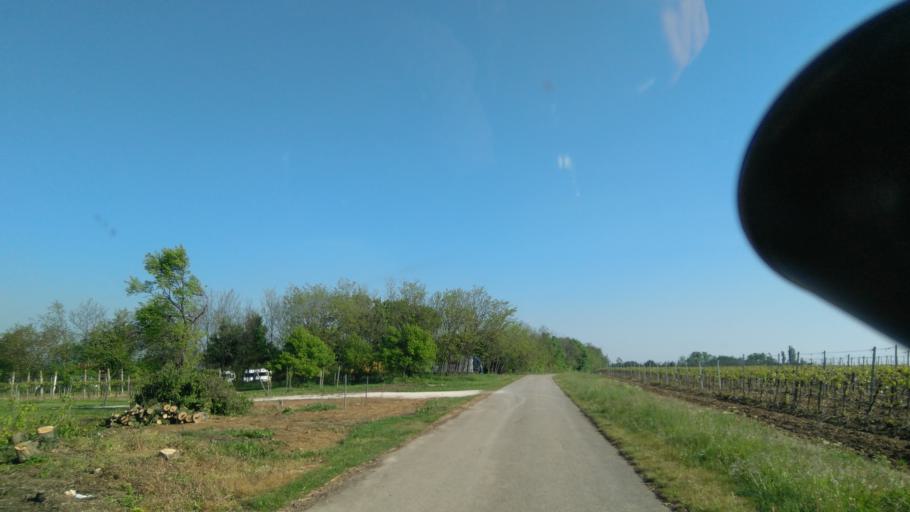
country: HU
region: Zala
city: Sarmellek
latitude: 46.7530
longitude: 17.1411
